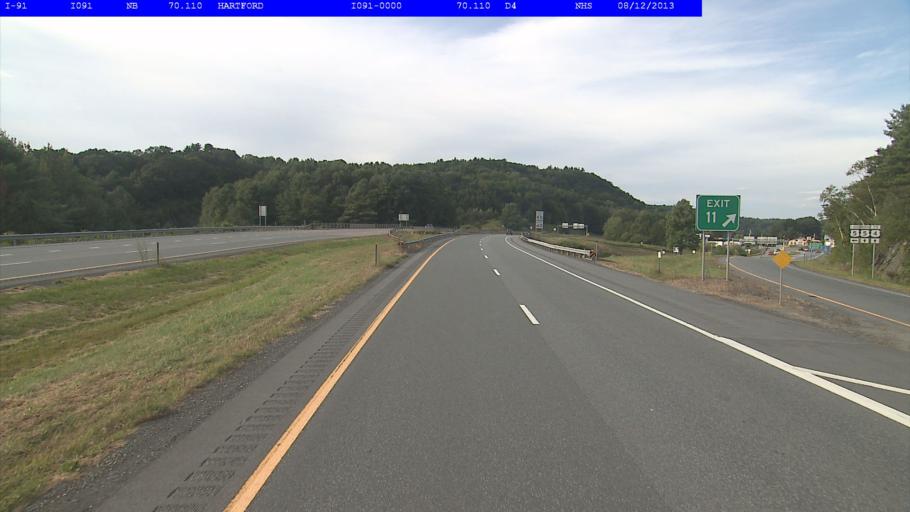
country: US
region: Vermont
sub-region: Windsor County
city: White River Junction
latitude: 43.6442
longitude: -72.3381
